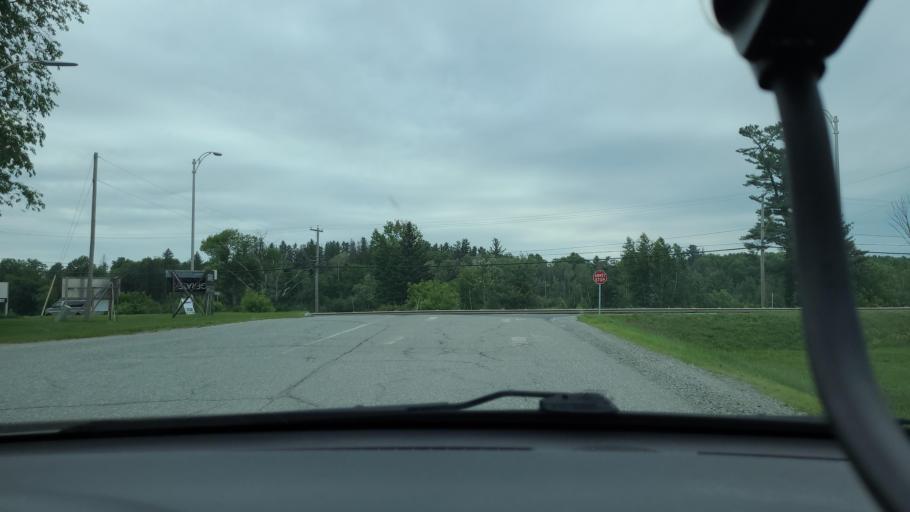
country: CA
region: Quebec
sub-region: Estrie
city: Sherbrooke
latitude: 45.3658
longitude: -71.8432
